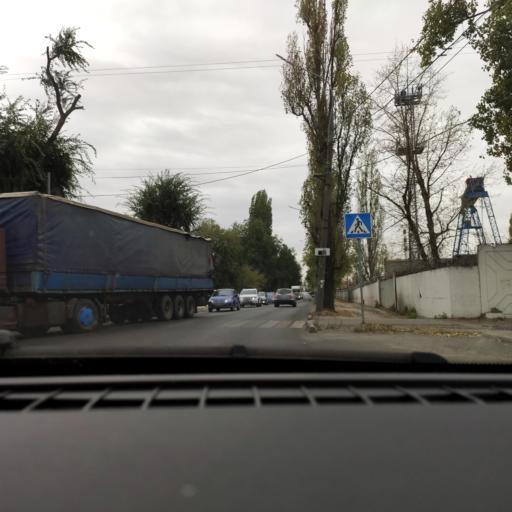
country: RU
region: Voronezj
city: Maslovka
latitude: 51.6340
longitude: 39.2633
